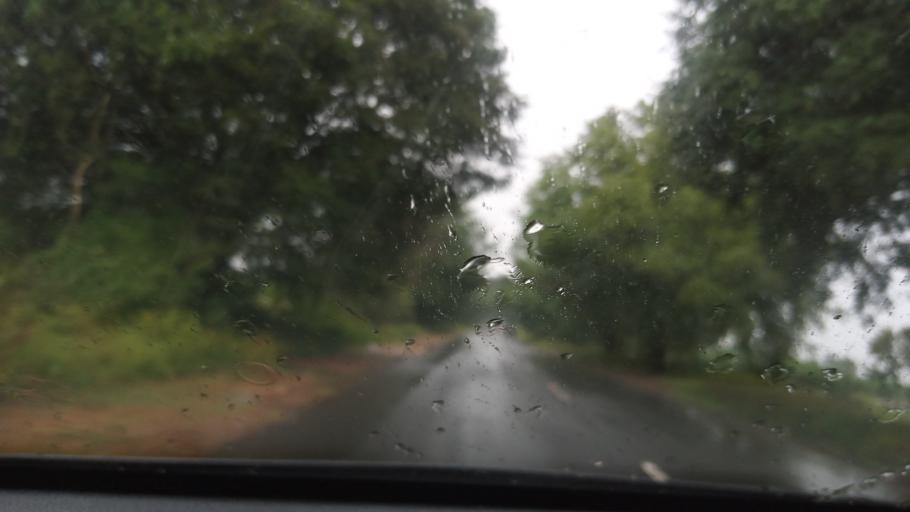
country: IN
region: Tamil Nadu
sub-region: Vellore
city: Kalavai
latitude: 12.8110
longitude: 79.4129
